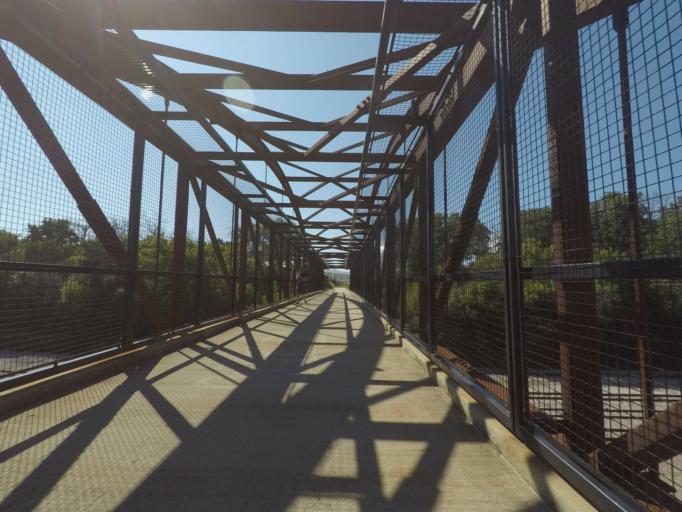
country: US
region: Wisconsin
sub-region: Milwaukee County
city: West Milwaukee
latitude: 43.0280
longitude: -87.9465
